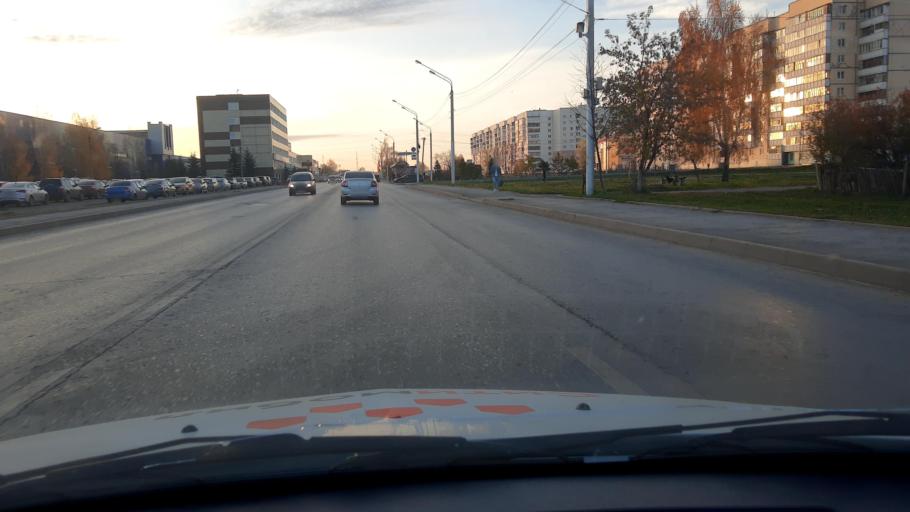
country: RU
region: Bashkortostan
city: Iglino
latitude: 54.7605
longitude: 56.2434
